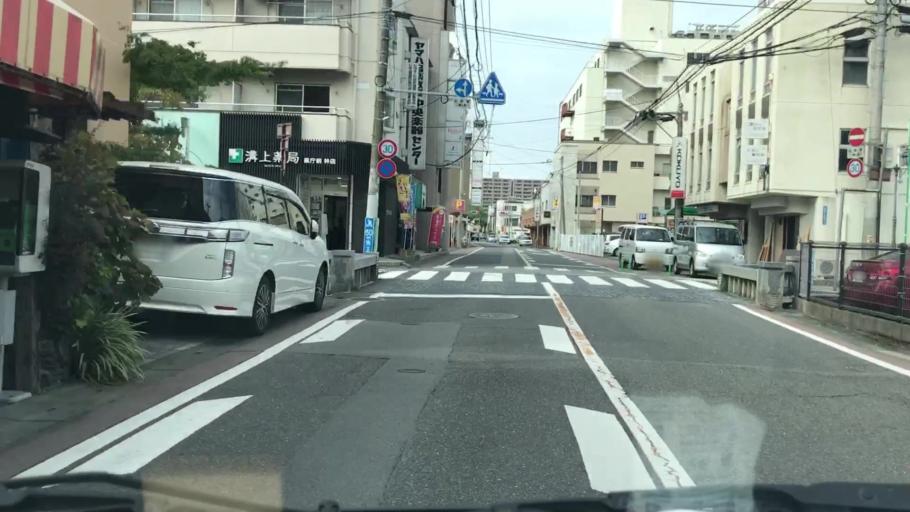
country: JP
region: Saga Prefecture
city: Saga-shi
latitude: 33.2513
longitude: 130.2993
